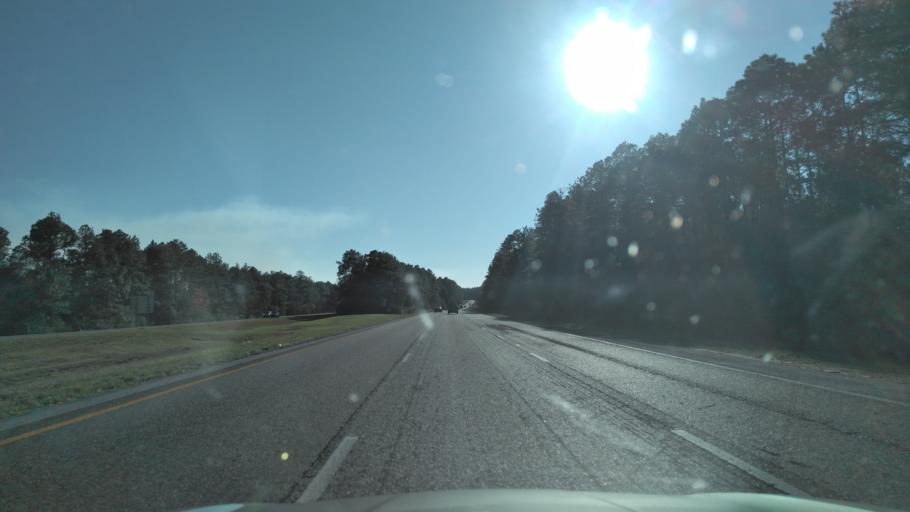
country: US
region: Alabama
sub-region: Escambia County
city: Atmore
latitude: 31.0162
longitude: -87.6606
